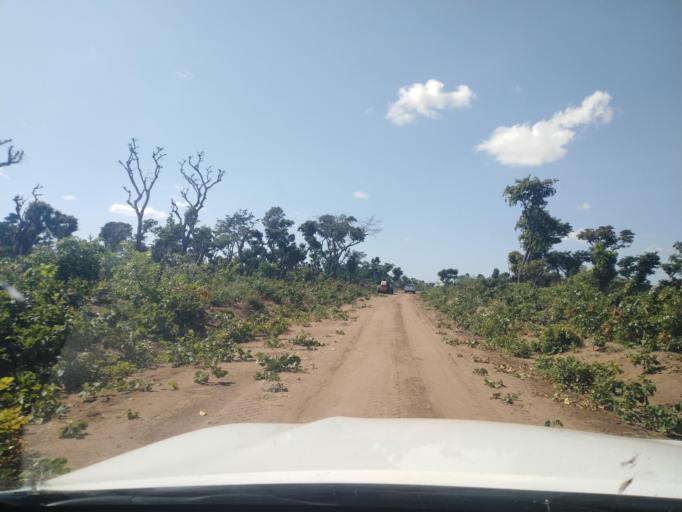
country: ZM
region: Northern
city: Chinsali
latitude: -11.0089
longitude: 31.7742
